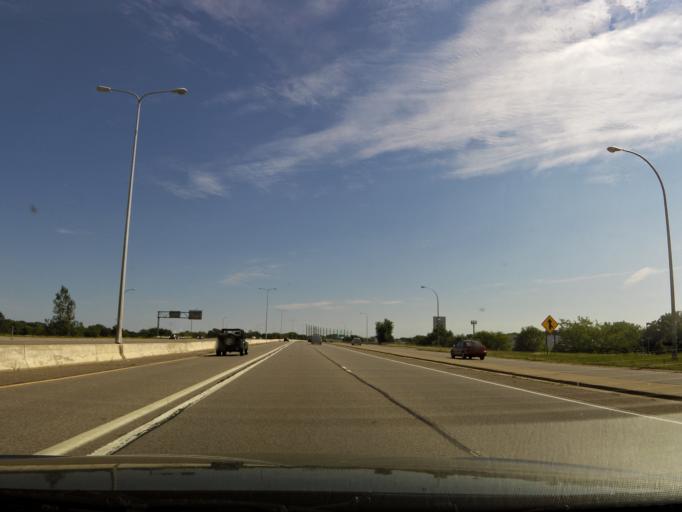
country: US
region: Minnesota
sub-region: Hennepin County
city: Minnetonka Mills
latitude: 44.9736
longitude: -93.3978
